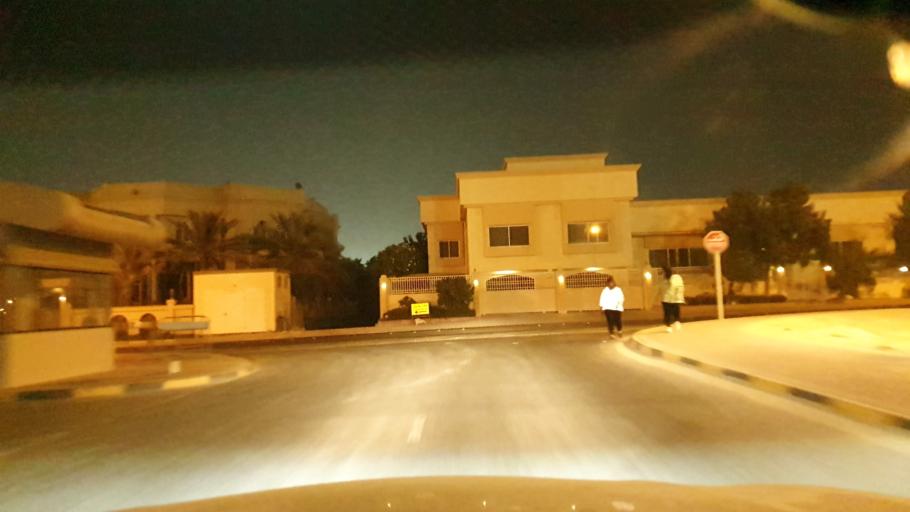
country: BH
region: Northern
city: Madinat `Isa
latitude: 26.1554
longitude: 50.5483
